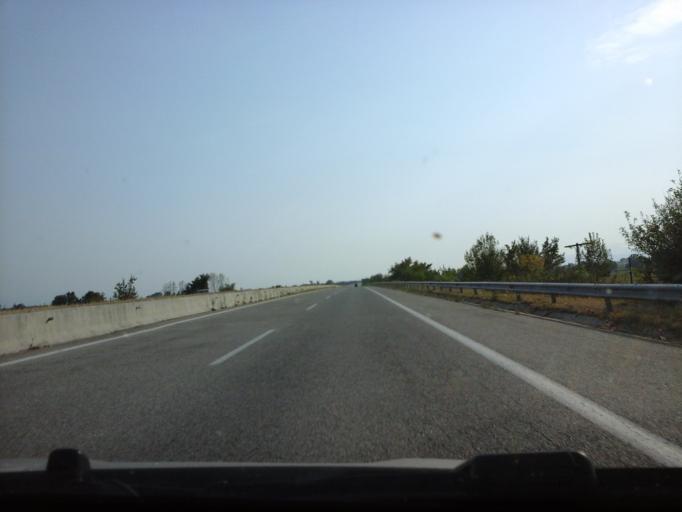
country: GR
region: East Macedonia and Thrace
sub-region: Nomos Xanthis
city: Selero
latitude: 41.1077
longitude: 24.9667
